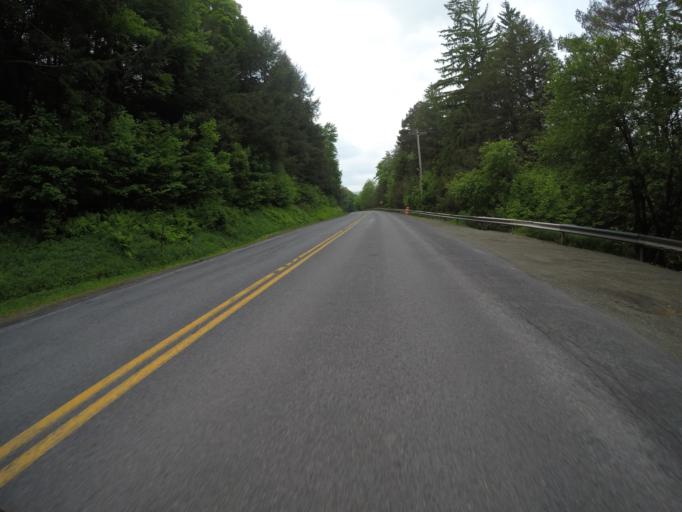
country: US
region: New York
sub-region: Delaware County
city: Delhi
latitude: 42.2541
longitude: -74.7970
